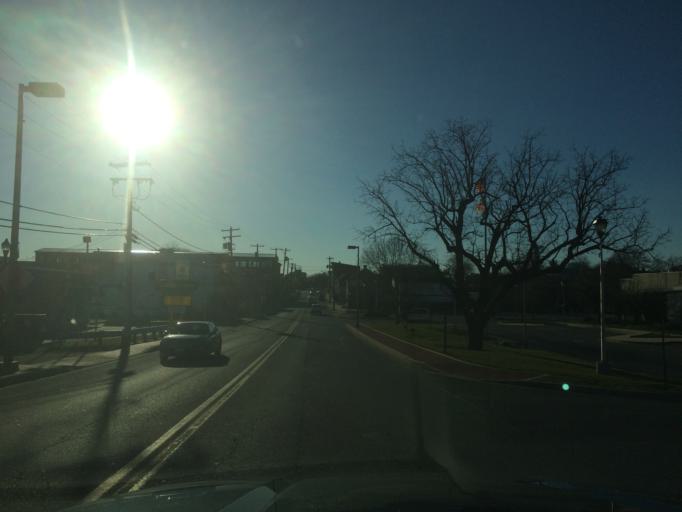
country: US
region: Maryland
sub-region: Frederick County
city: Frederick
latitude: 39.4136
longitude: -77.4015
